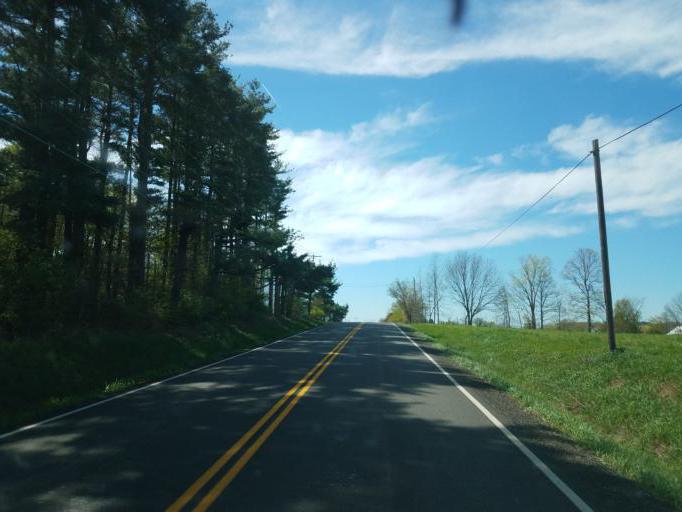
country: US
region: Ohio
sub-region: Huron County
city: Greenwich
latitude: 40.9149
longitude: -82.5071
